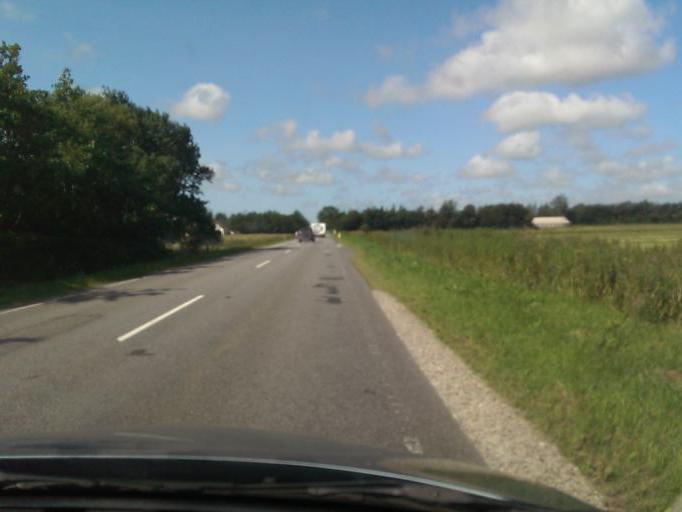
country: DK
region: North Denmark
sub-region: Bronderslev Kommune
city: Bronderslev
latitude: 57.2076
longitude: 9.8831
